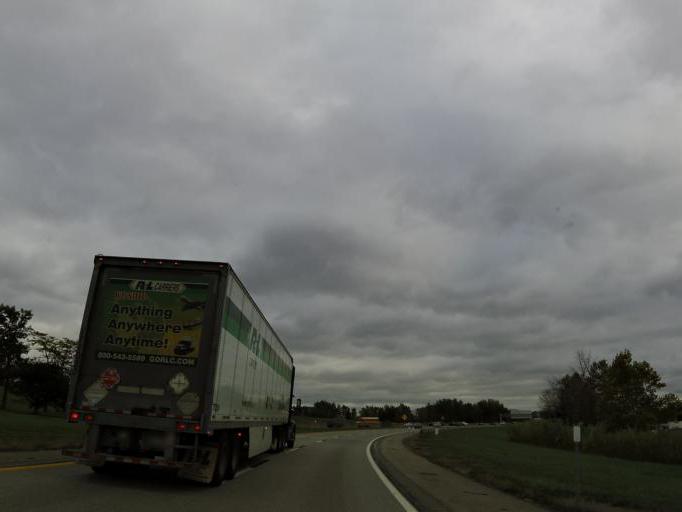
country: US
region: New York
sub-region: Erie County
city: Sloan
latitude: 42.8747
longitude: -78.7903
